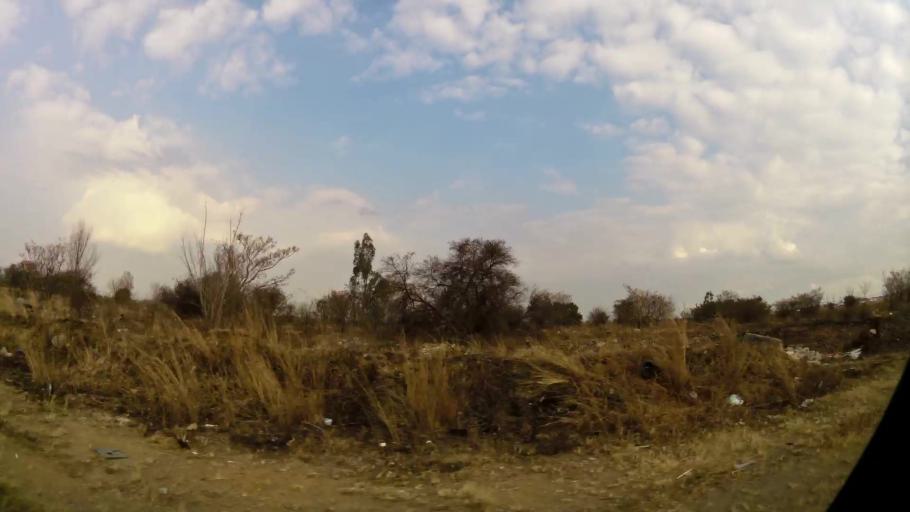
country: ZA
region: Gauteng
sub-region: Sedibeng District Municipality
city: Vereeniging
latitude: -26.6932
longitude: 27.8952
